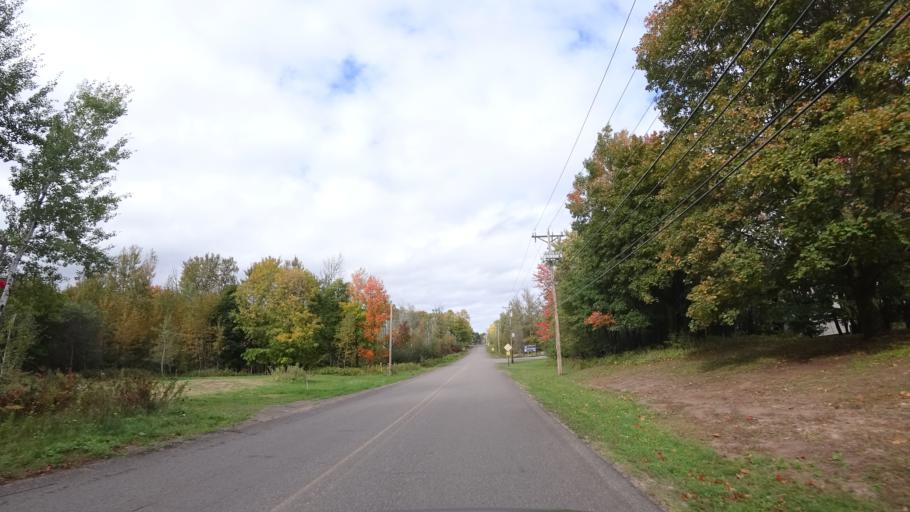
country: US
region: Michigan
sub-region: Marquette County
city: Trowbridge Park
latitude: 46.5439
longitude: -87.4374
